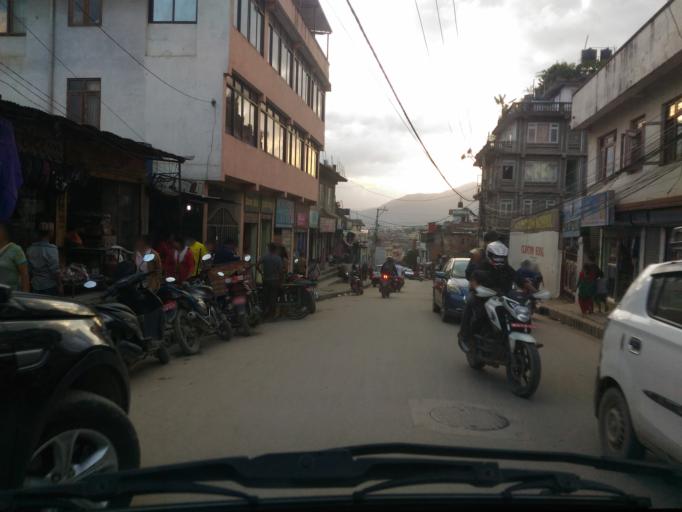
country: NP
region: Central Region
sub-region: Bagmati Zone
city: Kathmandu
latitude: 27.7170
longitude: 85.3441
